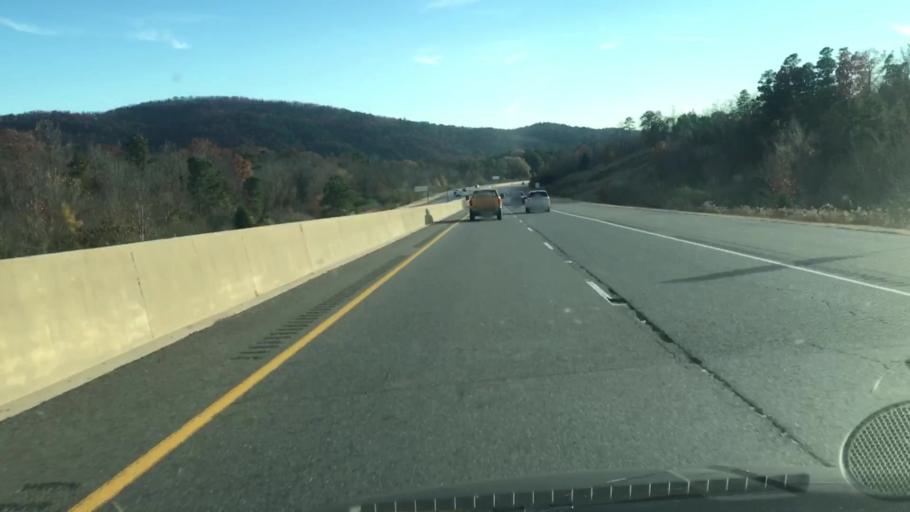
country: US
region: Arkansas
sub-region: Garland County
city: Hot Springs
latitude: 34.4987
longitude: -92.9756
